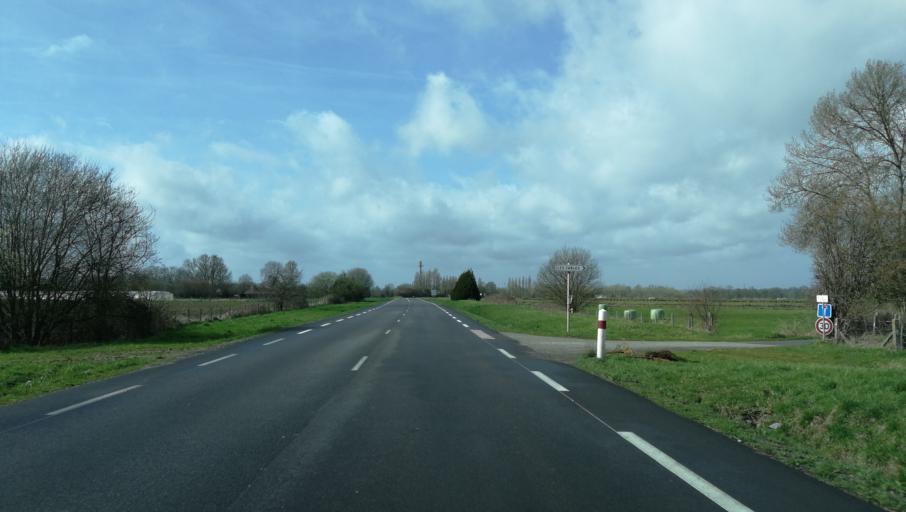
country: FR
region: Haute-Normandie
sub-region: Departement de l'Eure
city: Epaignes
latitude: 49.2850
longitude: 0.4117
